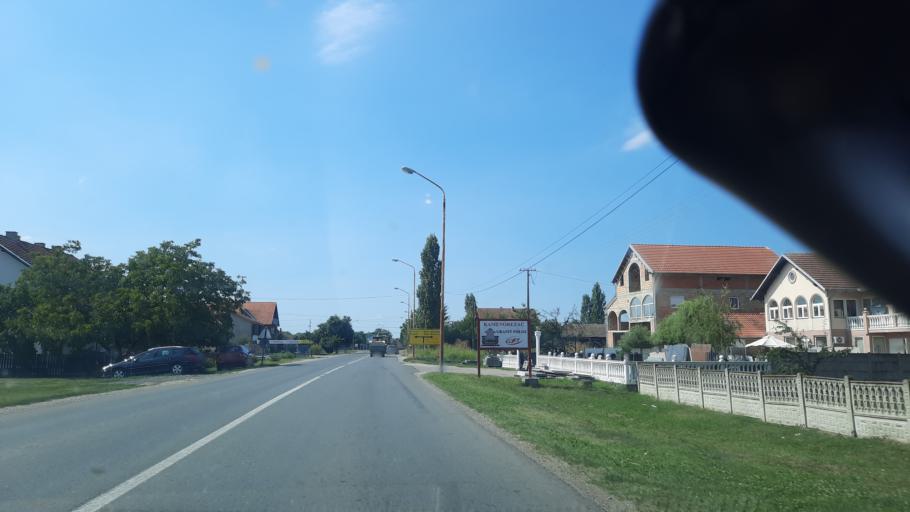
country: RS
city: Macvanska Mitrovica
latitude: 44.9551
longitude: 19.6021
